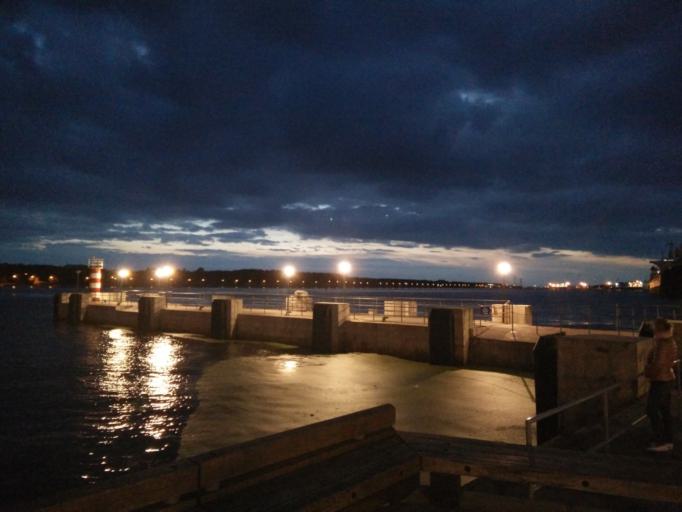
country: LT
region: Klaipedos apskritis
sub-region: Klaipeda
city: Klaipeda
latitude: 55.7062
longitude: 21.1230
